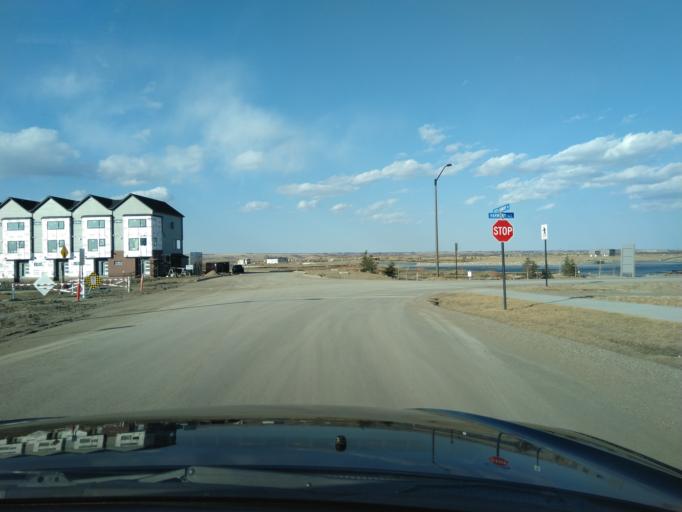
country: CA
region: Alberta
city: Cochrane
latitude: 51.1136
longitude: -114.3992
